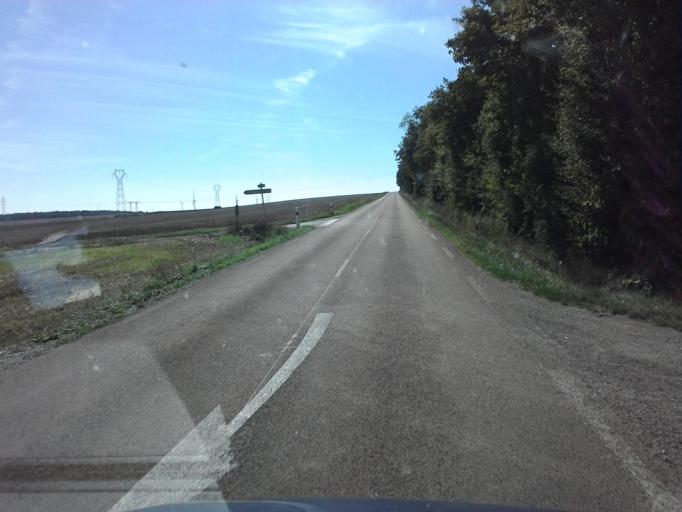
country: FR
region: Bourgogne
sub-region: Departement de l'Yonne
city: Tonnerre
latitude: 47.8117
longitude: 3.9564
